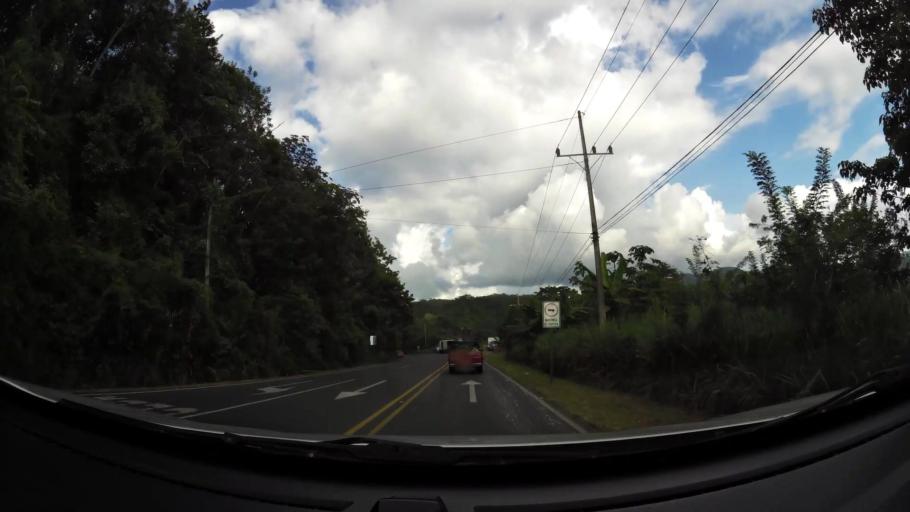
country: CR
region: Puntarenas
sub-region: Canton de Garabito
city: Jaco
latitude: 9.6891
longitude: -84.6452
